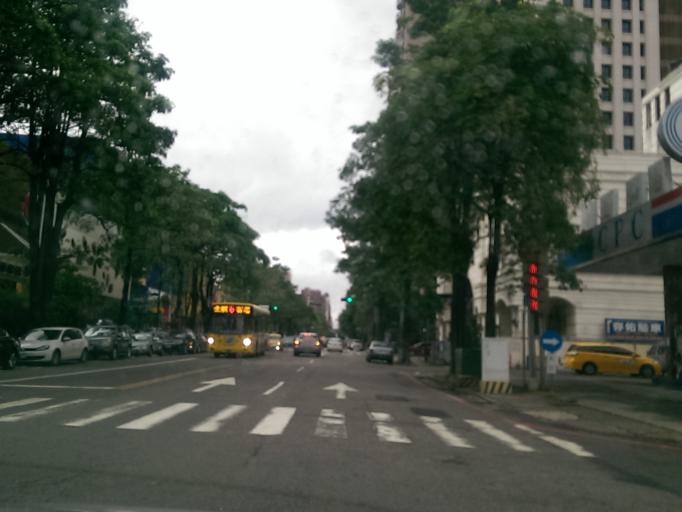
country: TW
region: Taiwan
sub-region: Taichung City
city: Taichung
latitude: 24.1468
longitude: 120.6418
